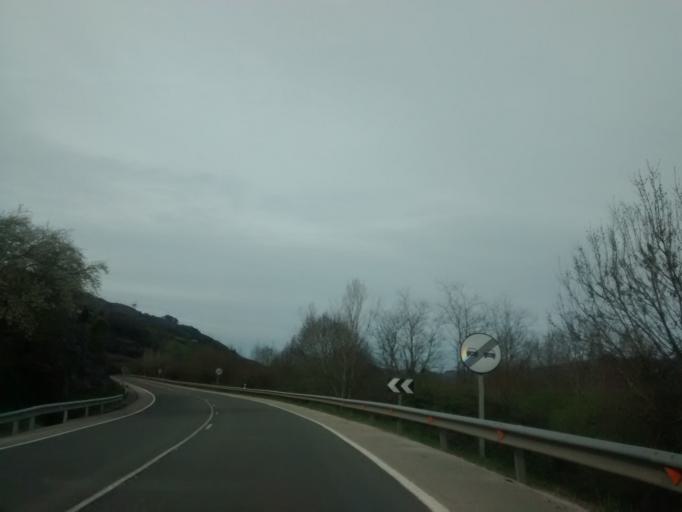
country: ES
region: Cantabria
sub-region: Provincia de Cantabria
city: Santiurde de Toranzo
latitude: 43.2230
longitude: -3.9448
